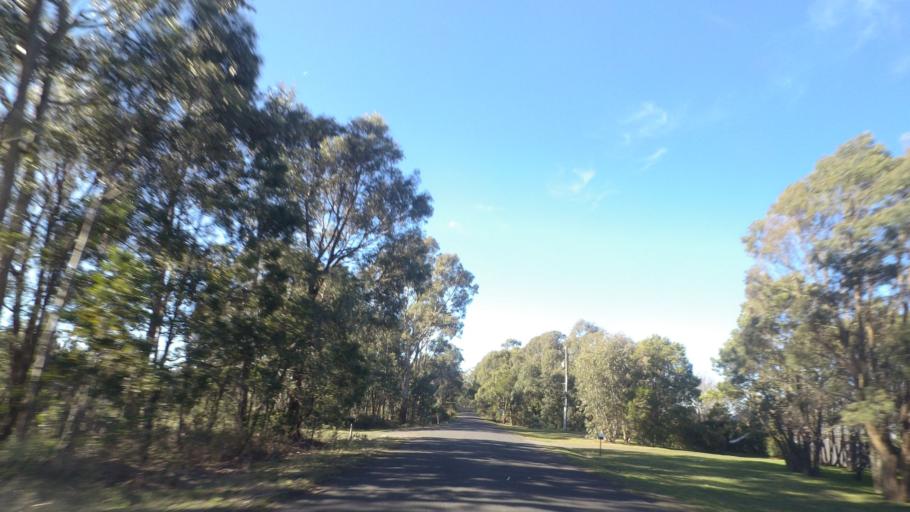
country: AU
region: Victoria
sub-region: Mount Alexander
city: Castlemaine
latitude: -37.3219
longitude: 144.3220
